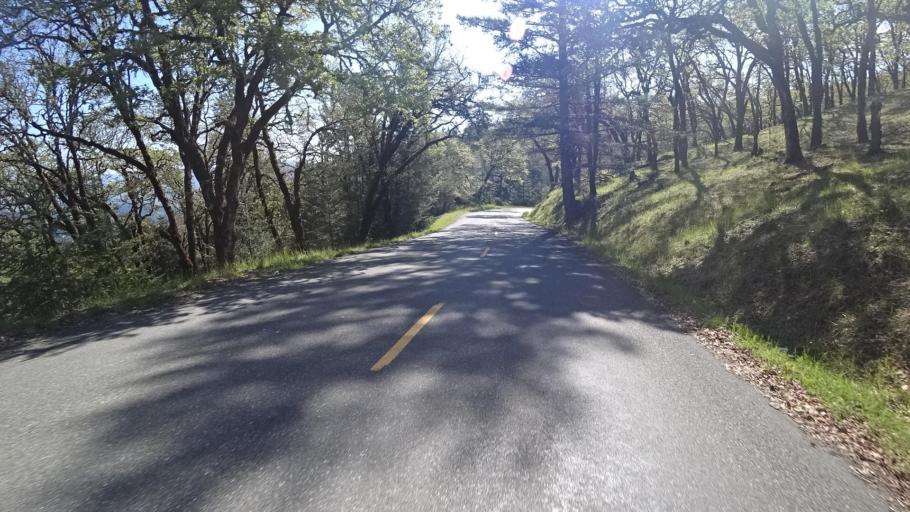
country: US
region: California
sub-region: Humboldt County
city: Redway
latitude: 40.0852
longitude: -123.6671
